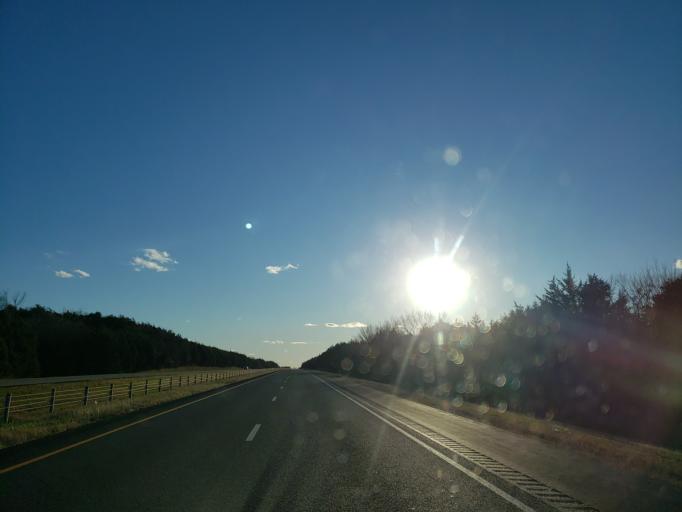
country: US
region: Alabama
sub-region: Sumter County
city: Livingston
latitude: 32.6659
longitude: -88.1775
